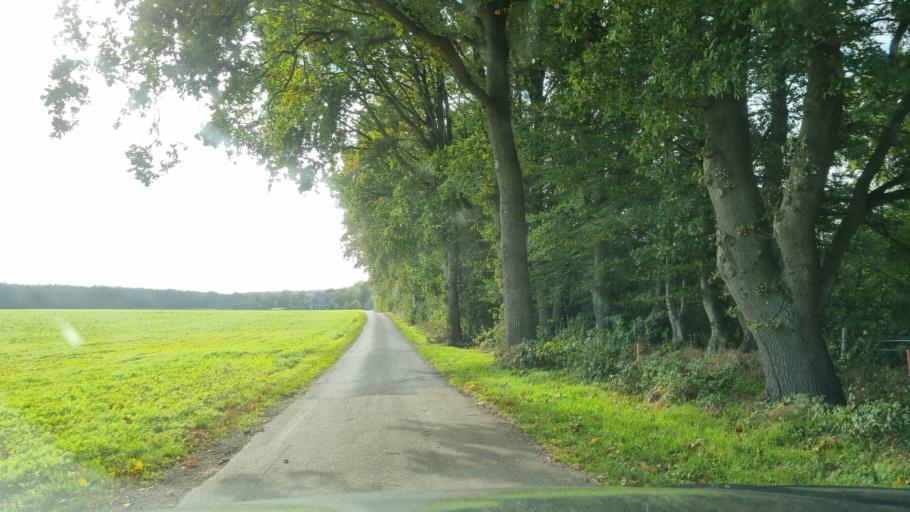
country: DE
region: North Rhine-Westphalia
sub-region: Regierungsbezirk Dusseldorf
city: Kranenburg
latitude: 51.7695
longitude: 6.0536
